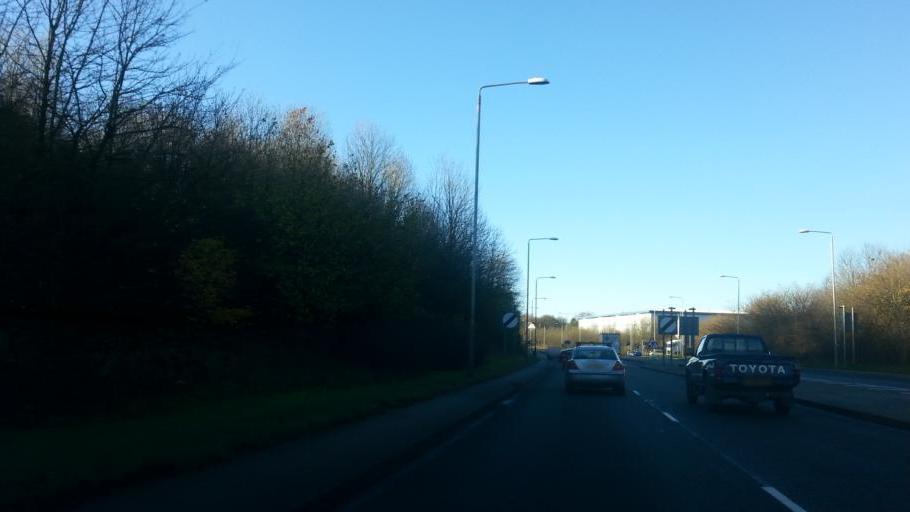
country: GB
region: England
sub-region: Nottinghamshire
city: Sutton in Ashfield
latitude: 53.1138
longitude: -1.2783
